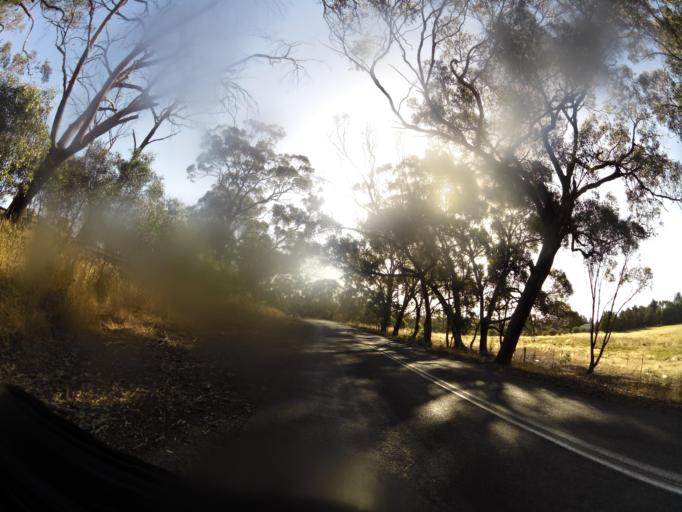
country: AU
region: Victoria
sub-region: Murrindindi
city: Kinglake West
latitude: -37.0115
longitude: 145.1201
